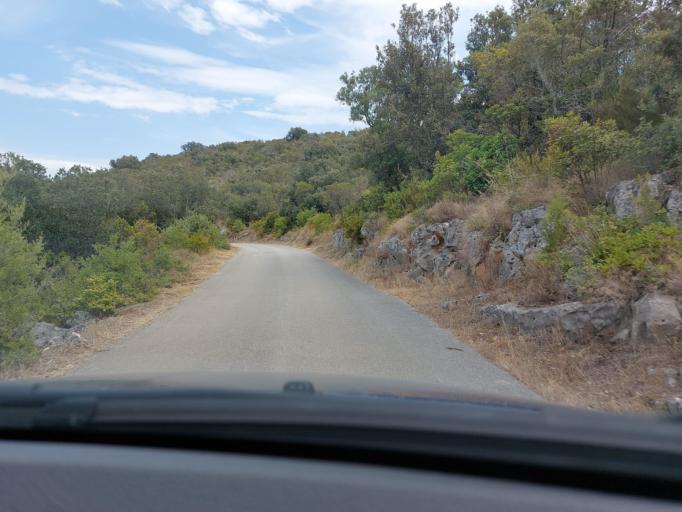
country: HR
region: Dubrovacko-Neretvanska
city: Smokvica
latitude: 42.7613
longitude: 16.9115
